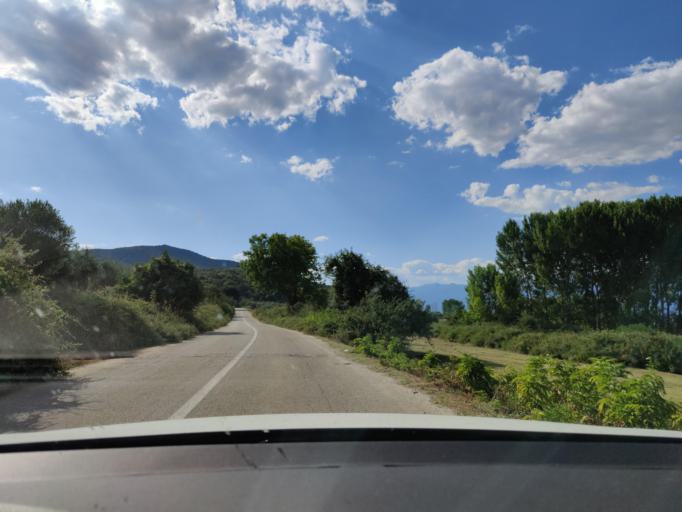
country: GR
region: Central Macedonia
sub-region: Nomos Serron
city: Chrysochorafa
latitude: 41.1608
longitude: 23.1889
